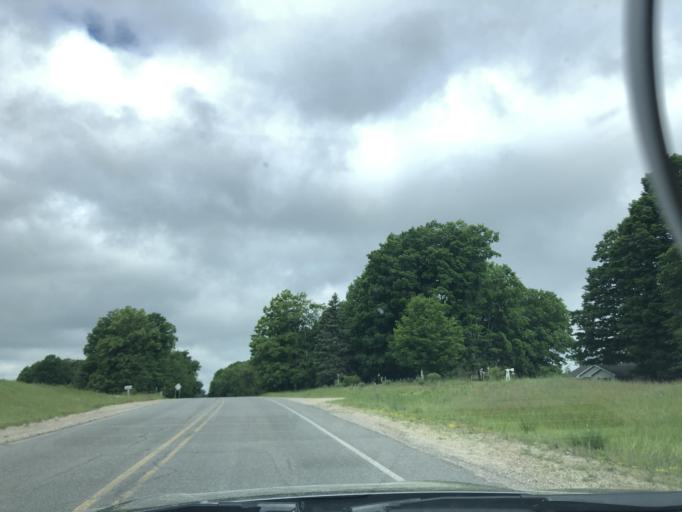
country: US
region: Michigan
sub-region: Missaukee County
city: Lake City
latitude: 44.4535
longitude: -85.2010
